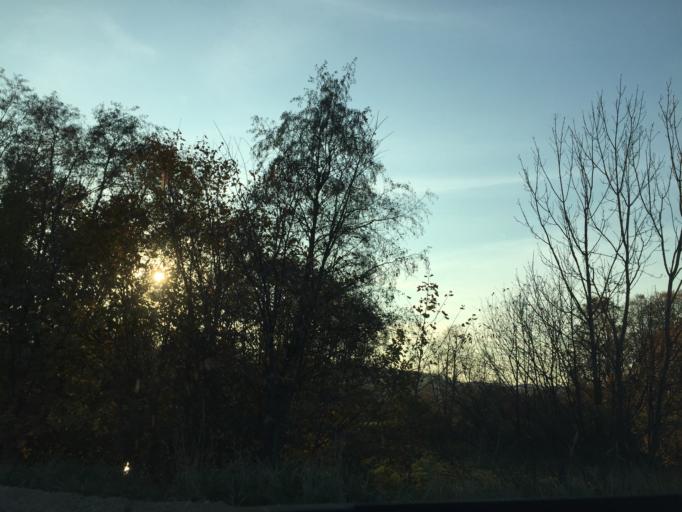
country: LV
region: Vainode
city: Vainode
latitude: 56.5148
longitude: 21.8294
